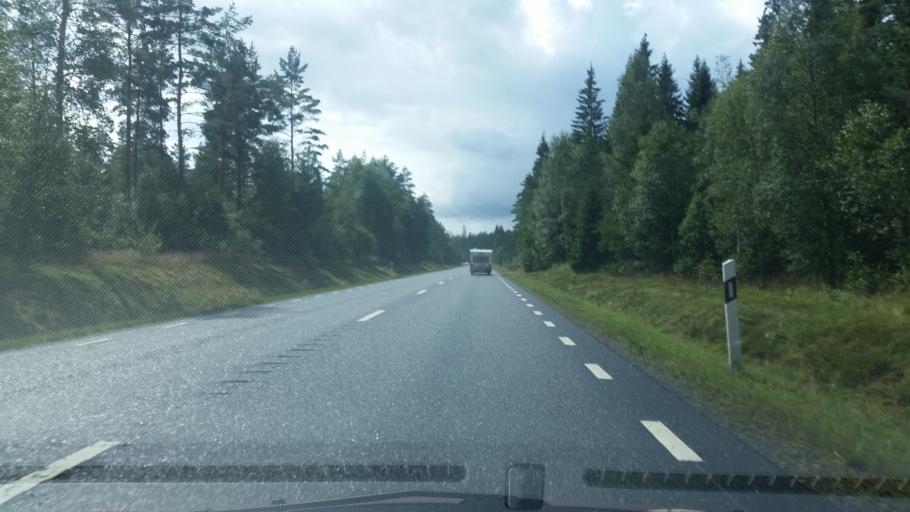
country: SE
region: Joenkoeping
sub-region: Gislaveds Kommun
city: Gislaved
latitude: 57.3843
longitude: 13.5833
